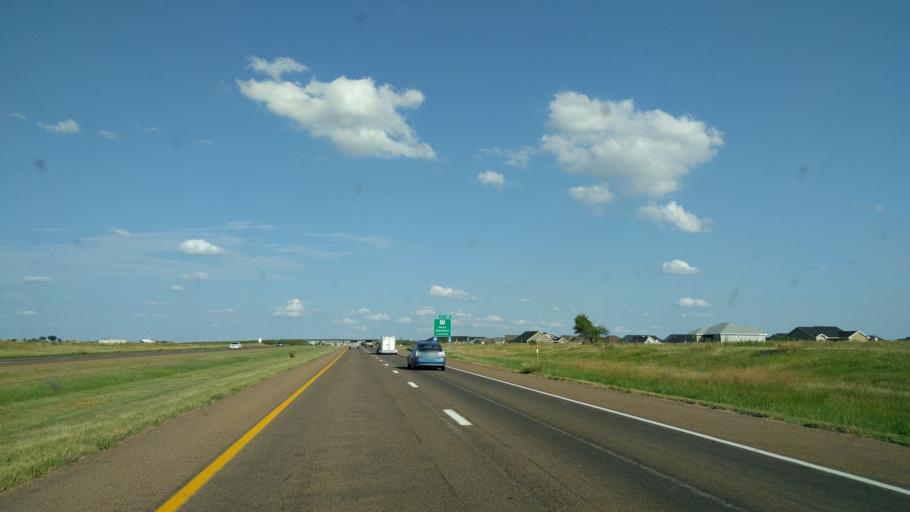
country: US
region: Kansas
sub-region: Ellis County
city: Hays
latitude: 38.9082
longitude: -99.3432
